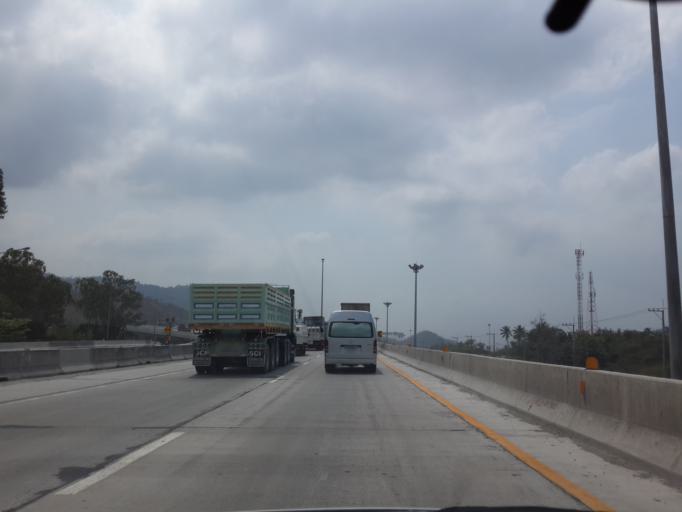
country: TH
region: Chon Buri
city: Chon Buri
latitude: 13.3045
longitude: 100.9940
